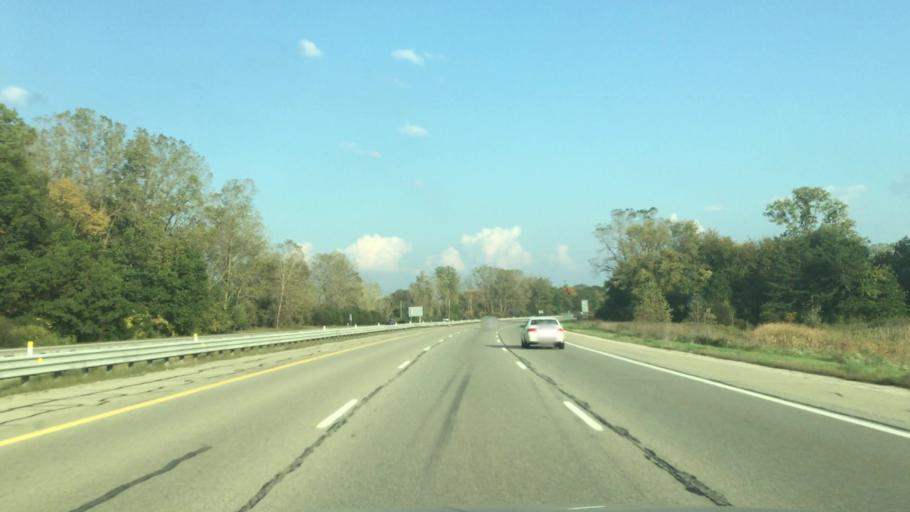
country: US
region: Michigan
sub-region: Washtenaw County
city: Dexter
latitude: 42.2990
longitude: -83.8633
